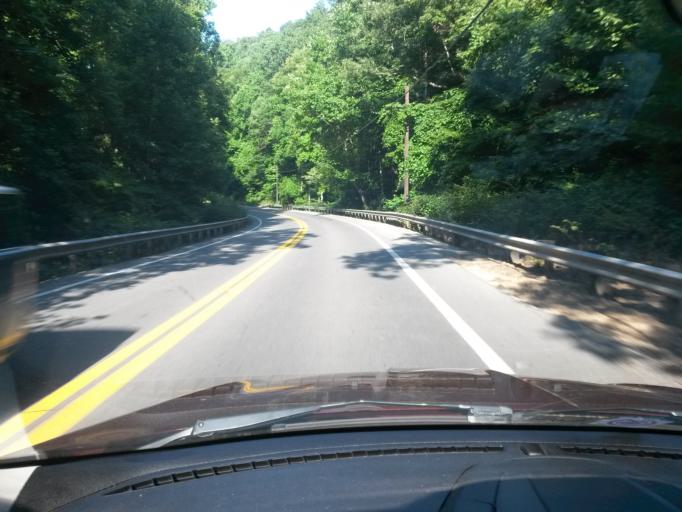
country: US
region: West Virginia
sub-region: Wyoming County
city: Pineville
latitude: 37.5613
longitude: -81.5386
